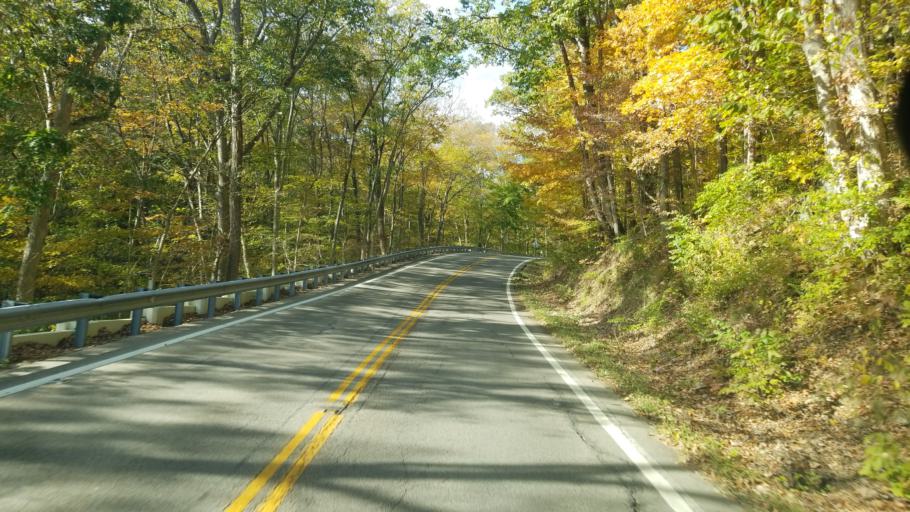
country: US
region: Ohio
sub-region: Clinton County
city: Blanchester
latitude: 39.3996
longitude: -84.0061
